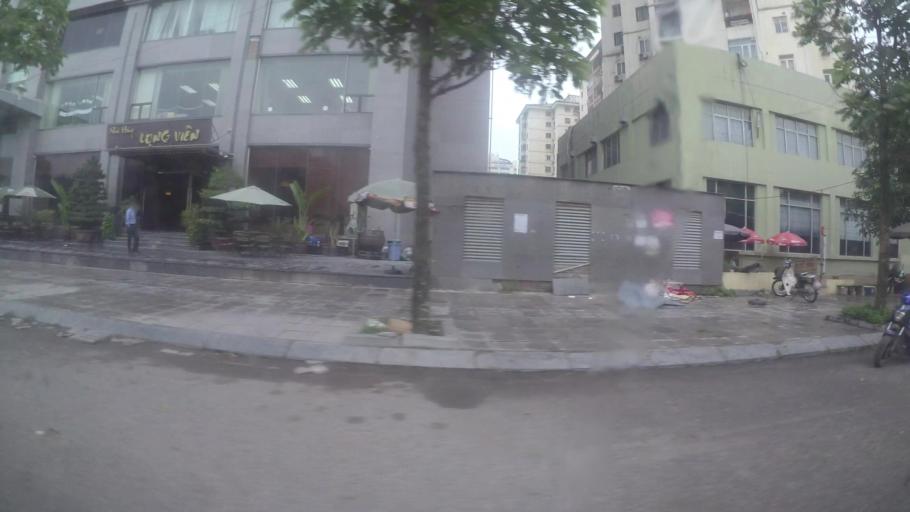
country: VN
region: Ha Noi
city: Cau Giay
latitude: 21.0220
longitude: 105.7868
